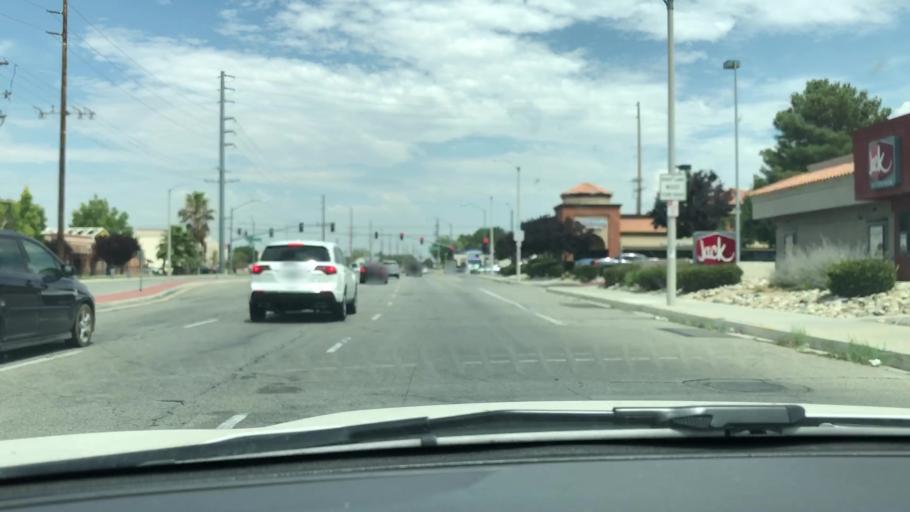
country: US
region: California
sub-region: Los Angeles County
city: Lancaster
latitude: 34.6748
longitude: -118.1672
